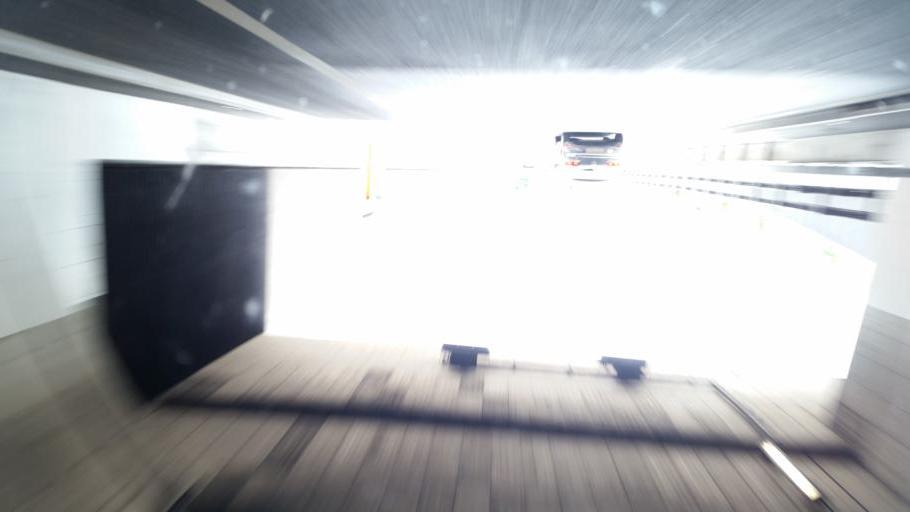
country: CH
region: Neuchatel
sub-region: Boudry District
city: Boudry
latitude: 46.9502
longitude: 6.8438
